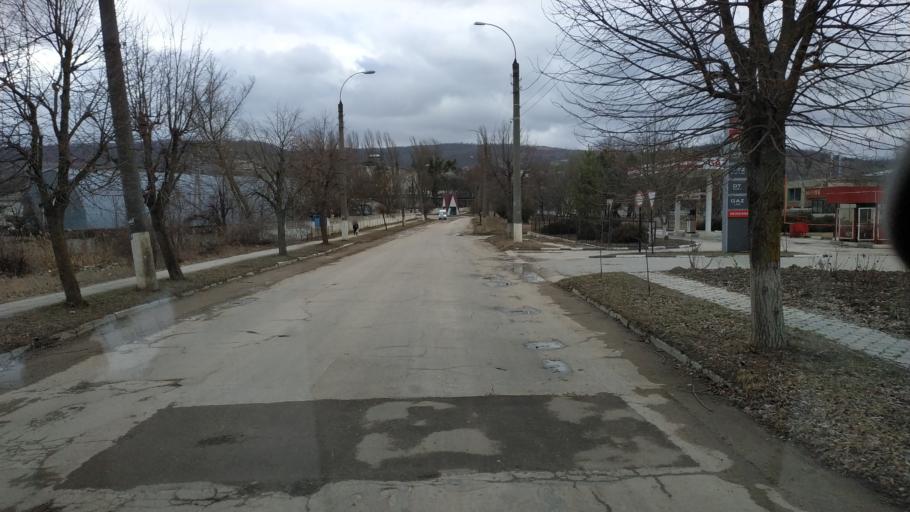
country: MD
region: Calarasi
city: Calarasi
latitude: 47.2445
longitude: 28.3149
